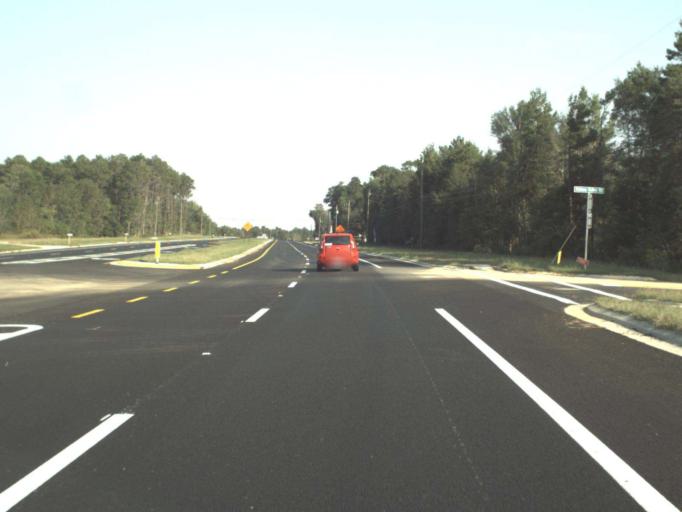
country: US
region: Florida
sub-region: Holmes County
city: Bonifay
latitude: 30.5713
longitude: -85.8068
